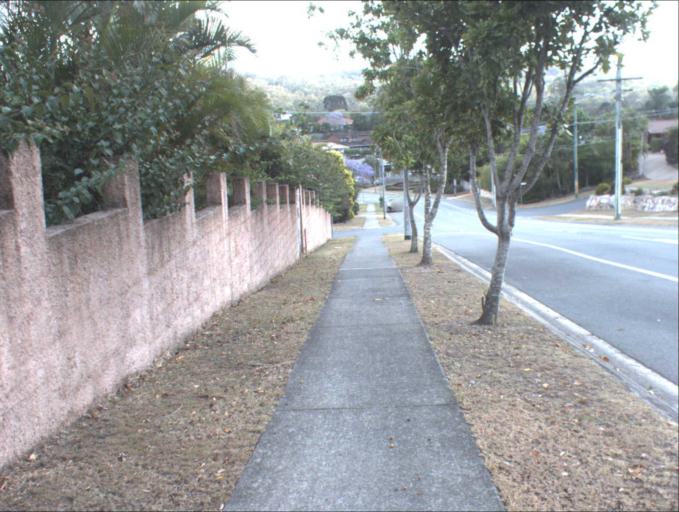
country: AU
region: Queensland
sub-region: Logan
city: Slacks Creek
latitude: -27.6570
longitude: 153.1882
